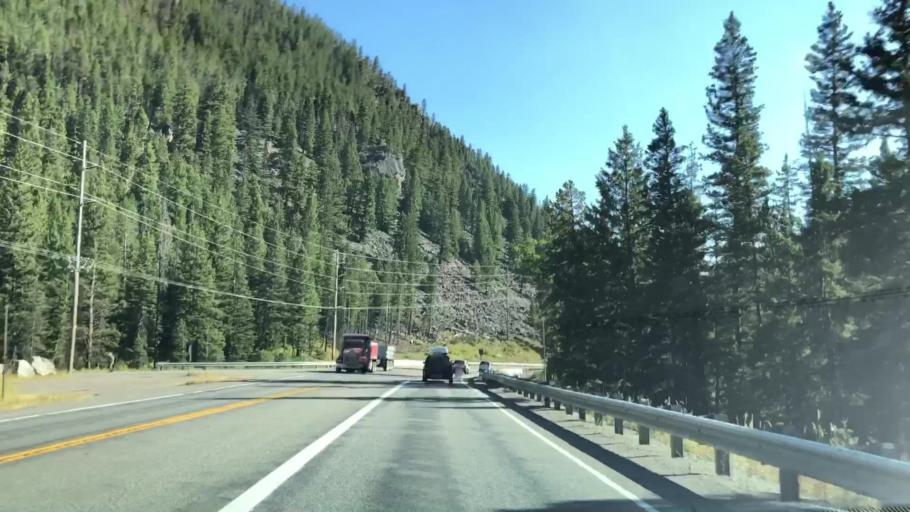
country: US
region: Montana
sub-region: Gallatin County
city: Big Sky
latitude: 45.3726
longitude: -111.1751
